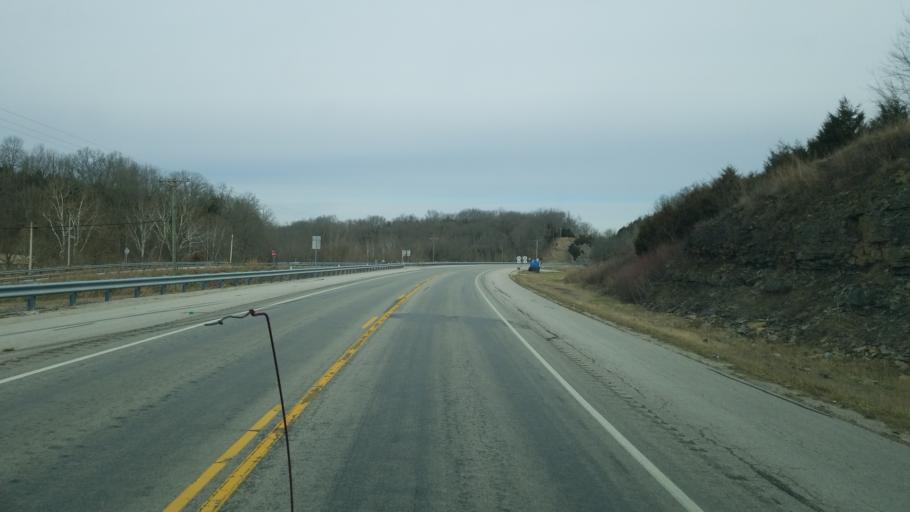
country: US
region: Kentucky
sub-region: Nicholas County
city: Carlisle
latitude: 38.4075
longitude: -84.0128
